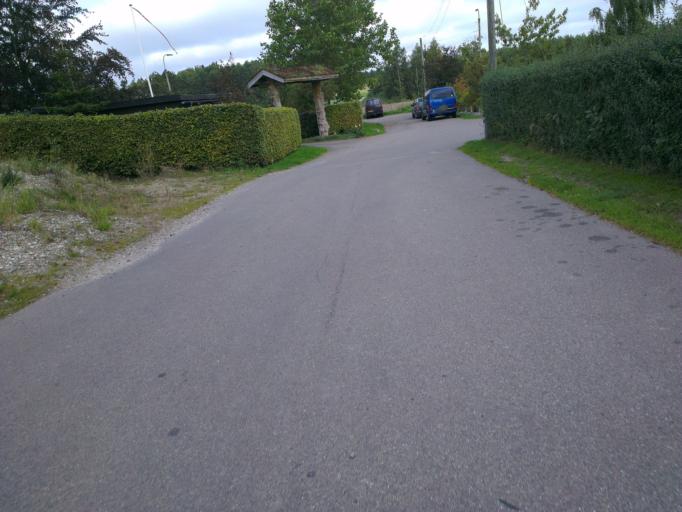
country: DK
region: Capital Region
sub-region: Frederikssund Kommune
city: Jaegerspris
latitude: 55.8180
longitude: 12.0068
